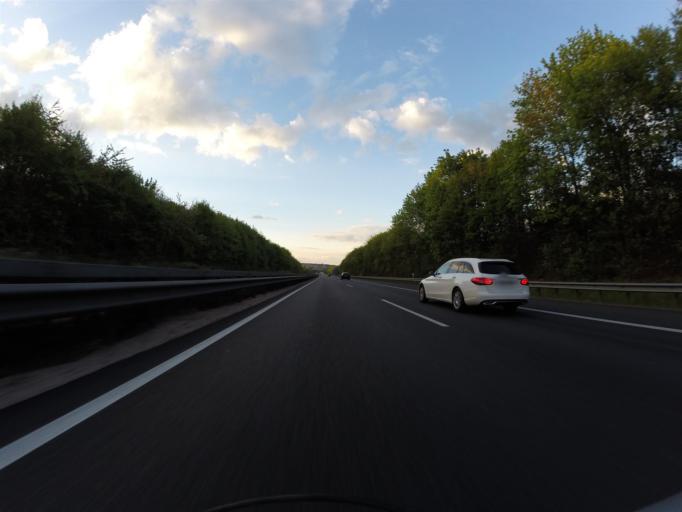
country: DE
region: Rheinland-Pfalz
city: Nieder-Olm
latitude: 49.9067
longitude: 8.1917
